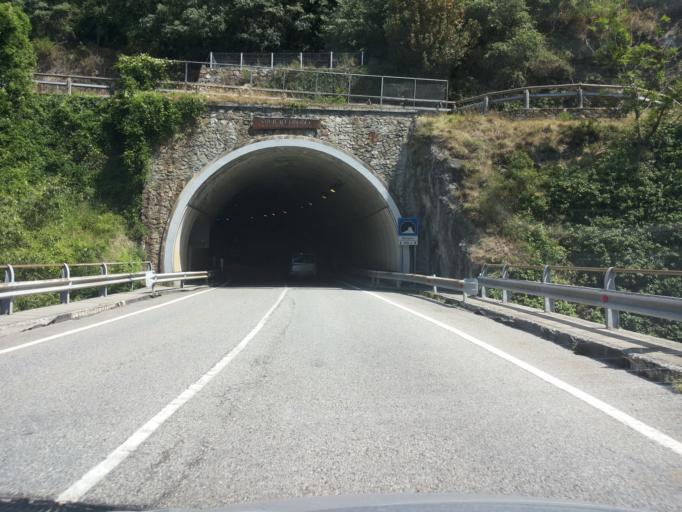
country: IT
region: Aosta Valley
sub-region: Valle d'Aosta
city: Perloz
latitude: 45.6108
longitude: 7.8157
